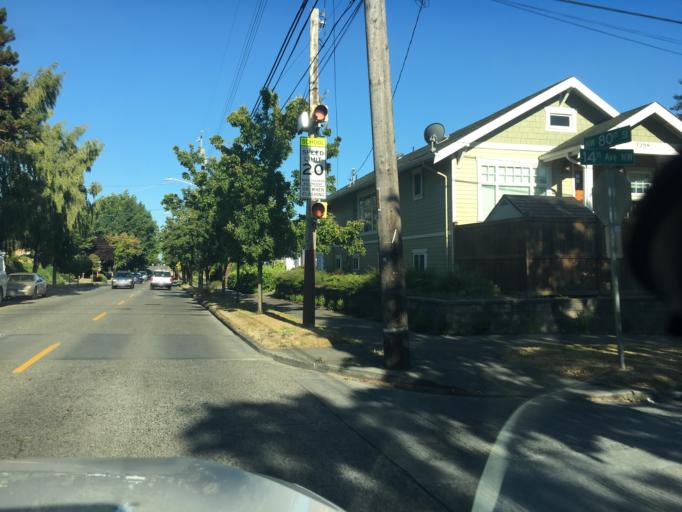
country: US
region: Washington
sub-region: King County
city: Shoreline
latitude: 47.6869
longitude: -122.3742
